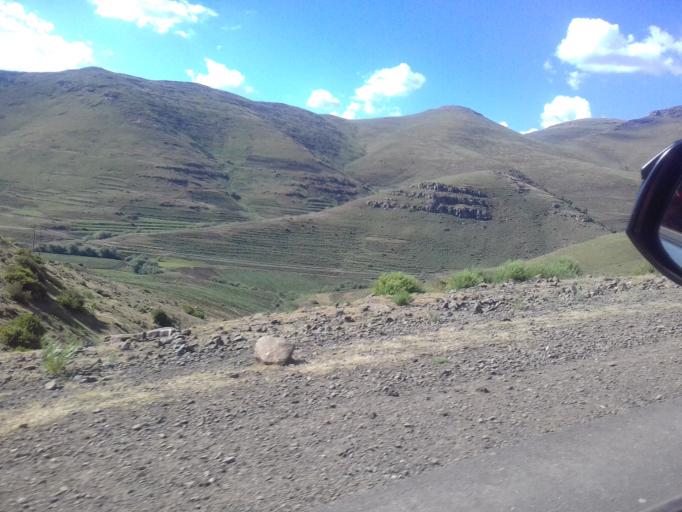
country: LS
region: Thaba-Tseka
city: Thaba-Tseka
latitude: -29.5145
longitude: 28.3213
